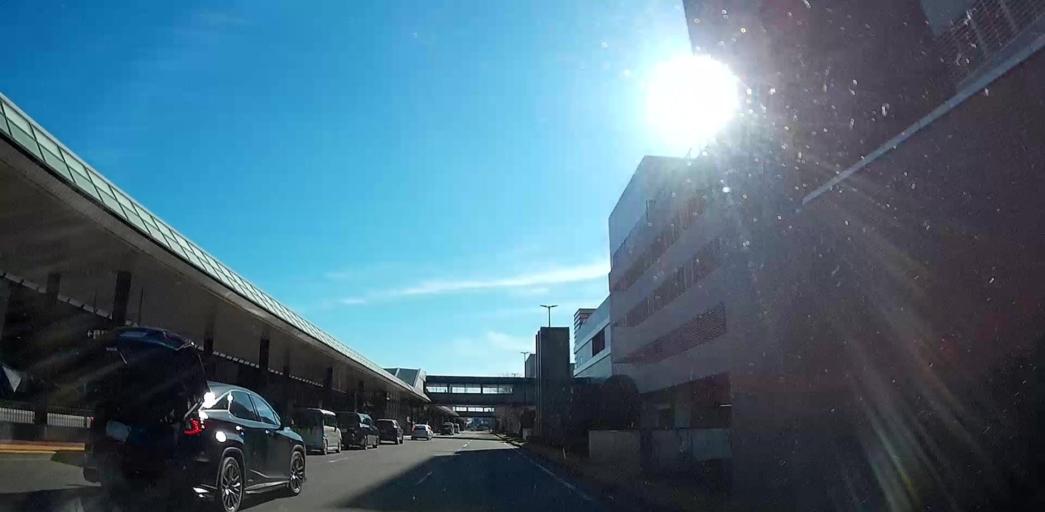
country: JP
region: Chiba
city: Narita
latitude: 35.7742
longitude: 140.3866
